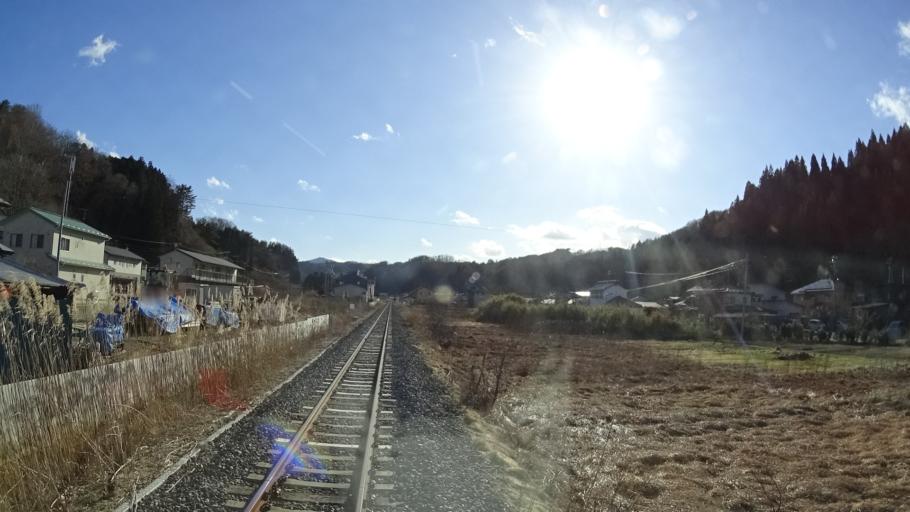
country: JP
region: Iwate
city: Miyako
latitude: 39.6176
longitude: 141.9440
